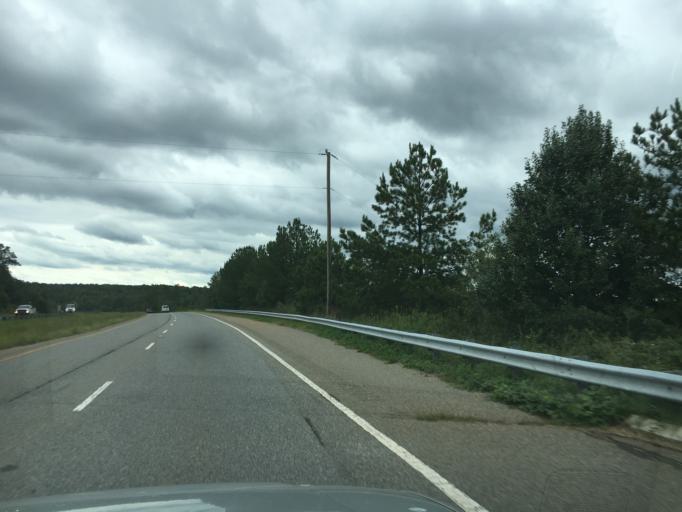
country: US
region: South Carolina
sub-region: Greenville County
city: Mauldin
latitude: 34.7181
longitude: -82.3573
